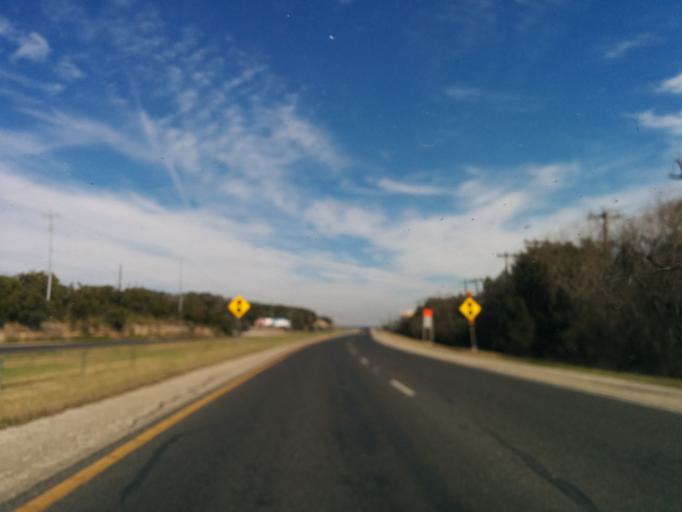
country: US
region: Texas
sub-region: Bexar County
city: Timberwood Park
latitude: 29.7074
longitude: -98.4499
